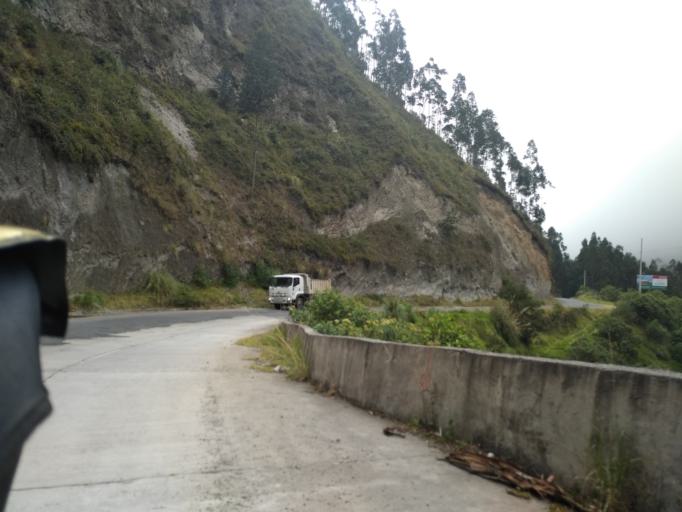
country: EC
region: Cotopaxi
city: Saquisili
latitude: -0.6936
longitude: -78.8195
